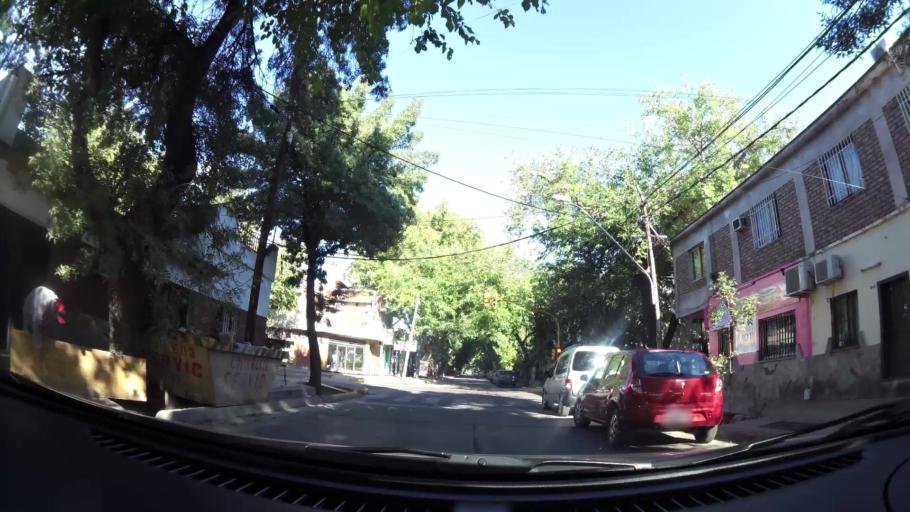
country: AR
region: Mendoza
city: Mendoza
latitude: -32.8741
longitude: -68.8305
